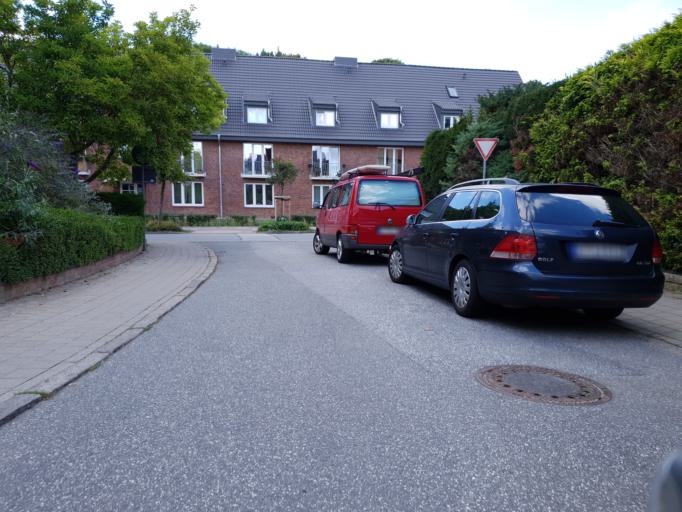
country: DE
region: Schleswig-Holstein
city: Kronshagen
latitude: 54.3327
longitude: 10.0892
